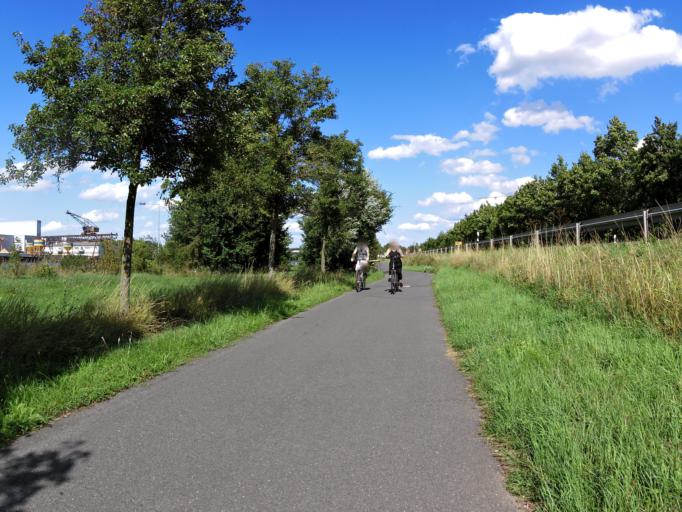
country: DE
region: Bavaria
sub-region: Regierungsbezirk Unterfranken
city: Kitzingen
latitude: 49.7210
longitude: 10.1587
